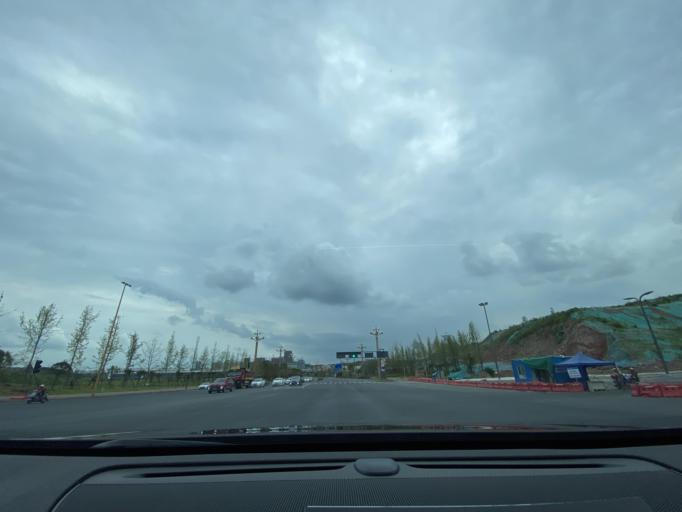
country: CN
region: Sichuan
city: Jiancheng
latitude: 30.4467
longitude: 104.4959
